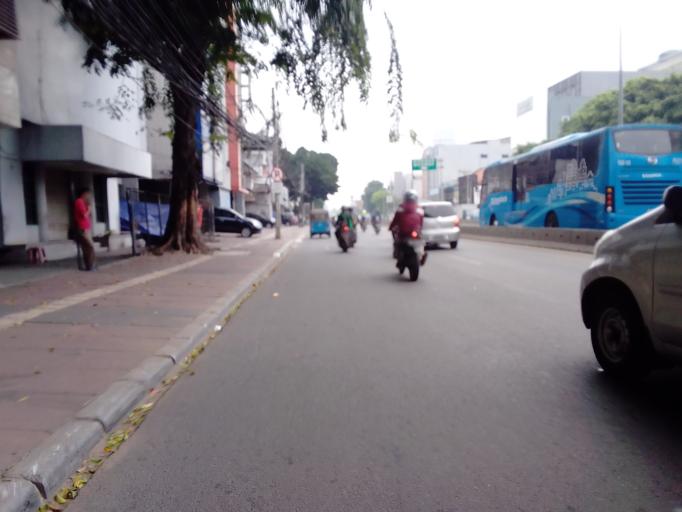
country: ID
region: Jakarta Raya
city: Jakarta
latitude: -6.1655
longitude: 106.8130
